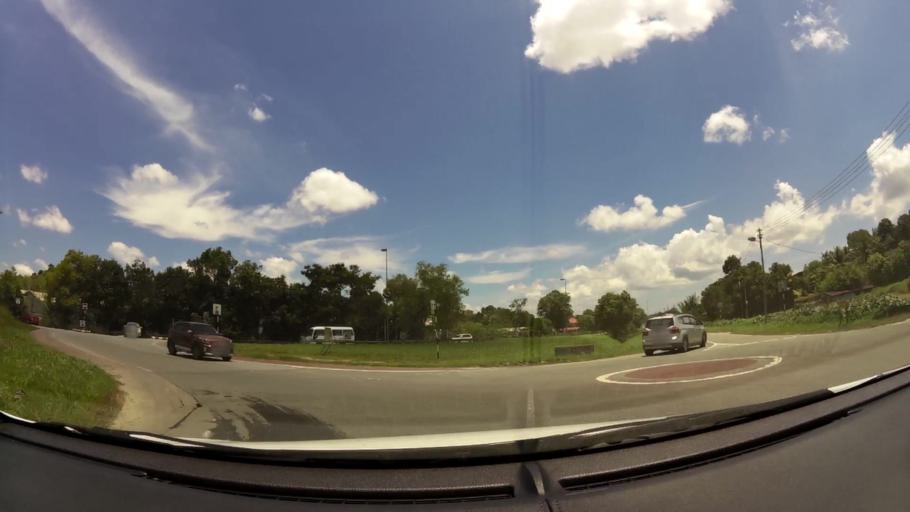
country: BN
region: Brunei and Muara
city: Bandar Seri Begawan
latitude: 4.9349
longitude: 114.9586
